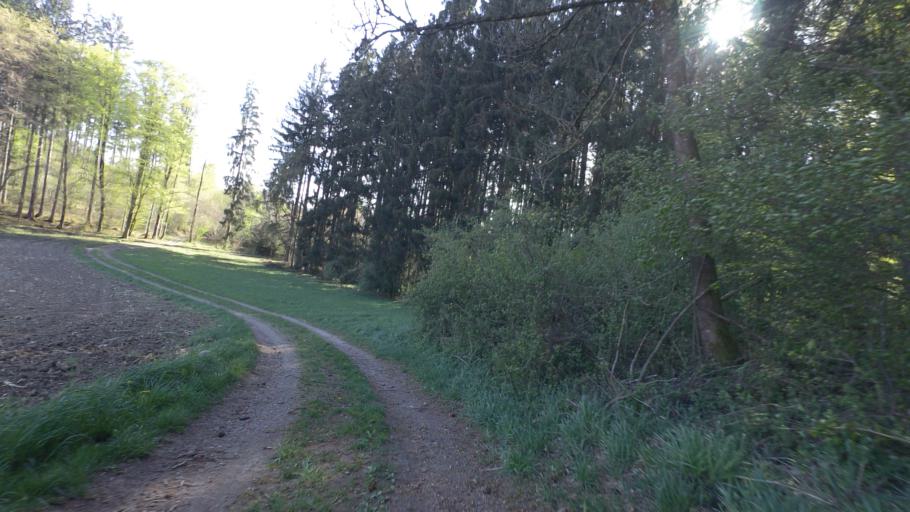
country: DE
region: Bavaria
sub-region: Upper Bavaria
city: Grabenstatt
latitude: 47.8620
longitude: 12.5685
